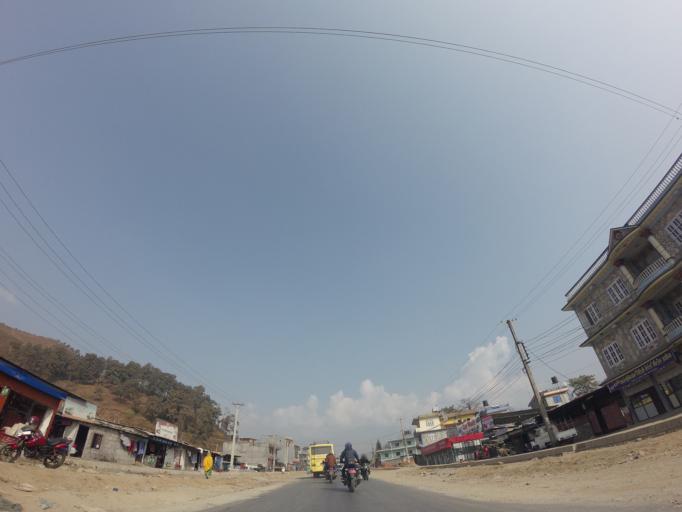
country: NP
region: Western Region
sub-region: Gandaki Zone
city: Pokhara
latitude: 28.2268
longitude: 83.9809
